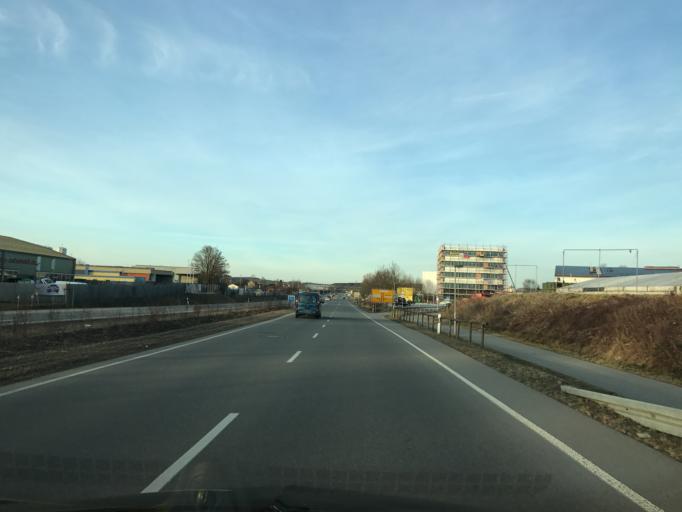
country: DE
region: Baden-Wuerttemberg
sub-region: Tuebingen Region
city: Friedrichshafen
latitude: 47.6675
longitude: 9.4956
